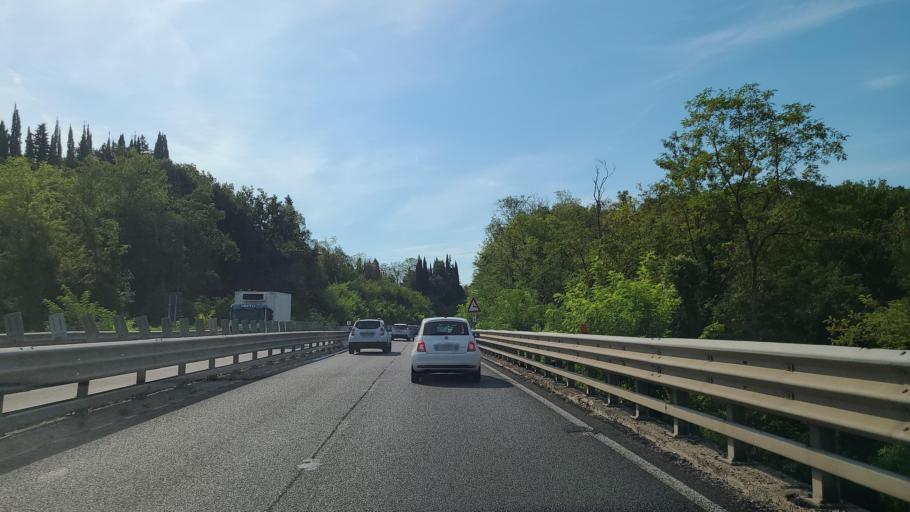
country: IT
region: Tuscany
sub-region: Province of Florence
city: Sambuca
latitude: 43.5676
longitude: 11.2114
